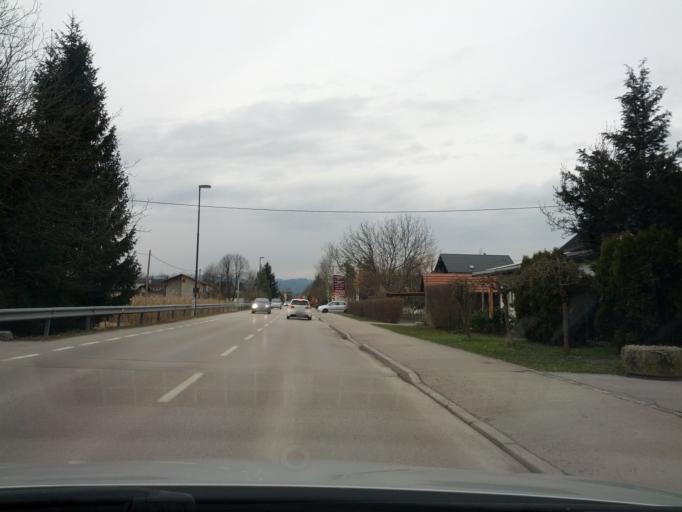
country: SI
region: Ljubljana
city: Ljubljana
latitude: 46.0307
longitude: 14.5188
